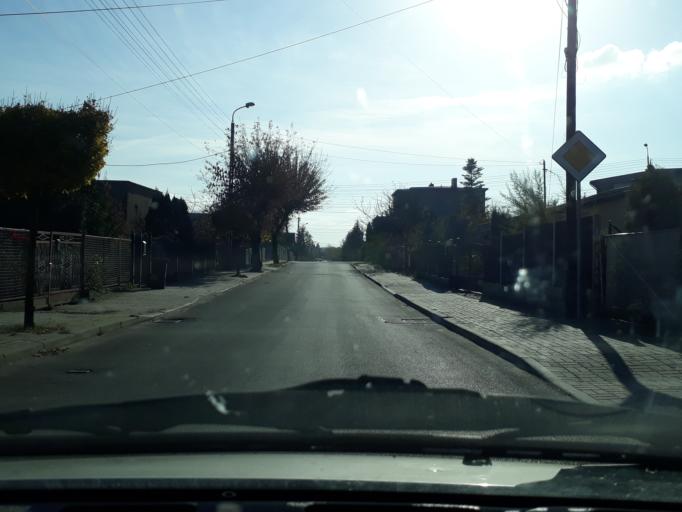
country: PL
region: Silesian Voivodeship
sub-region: Powiat tarnogorski
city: Tarnowskie Gory
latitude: 50.4324
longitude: 18.8442
